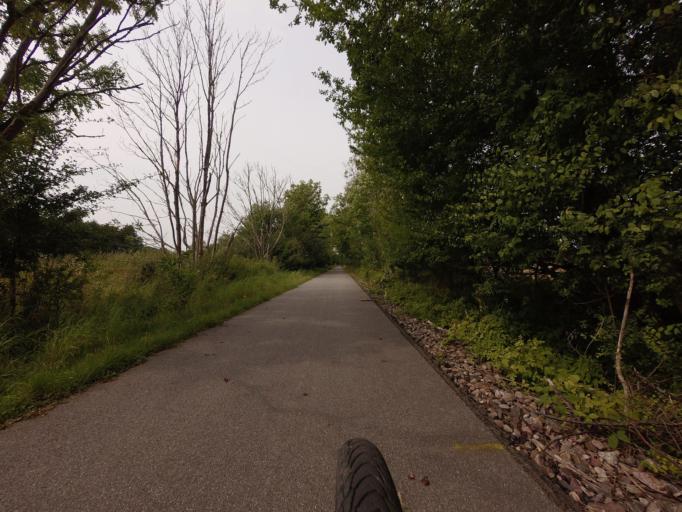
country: DK
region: Zealand
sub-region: Naestved Kommune
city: Fuglebjerg
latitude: 55.2611
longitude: 11.5773
